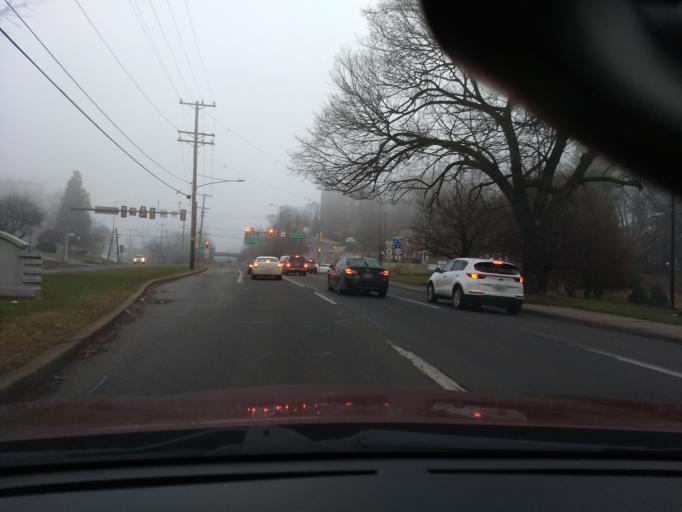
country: US
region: Pennsylvania
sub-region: Allegheny County
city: Braddock Hills
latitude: 40.4318
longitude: -79.8643
